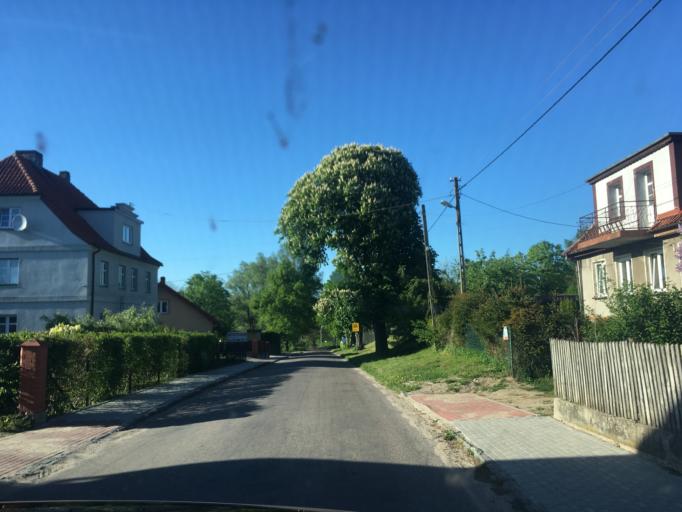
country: PL
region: Warmian-Masurian Voivodeship
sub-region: Powiat piski
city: Ruciane-Nida
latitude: 53.6858
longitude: 21.4999
